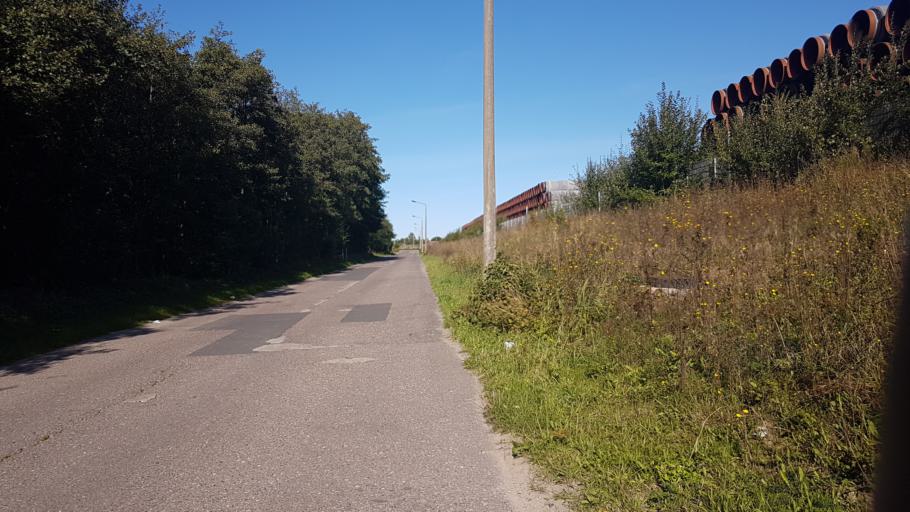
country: DE
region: Mecklenburg-Vorpommern
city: Sagard
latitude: 54.4899
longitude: 13.5725
